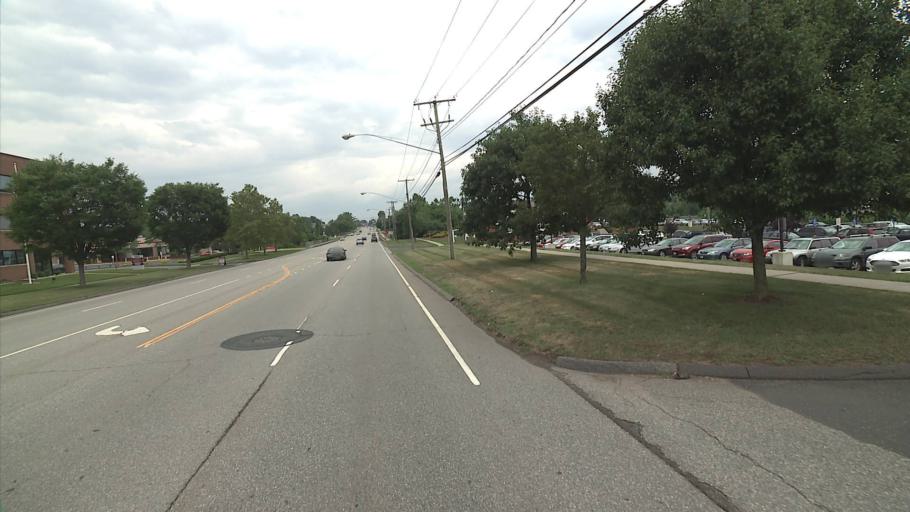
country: US
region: Connecticut
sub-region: Hartford County
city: Wethersfield
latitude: 41.6873
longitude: -72.6551
